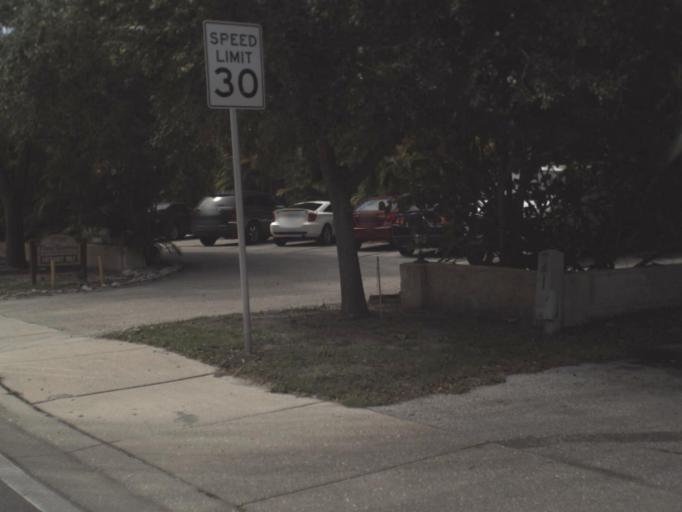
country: US
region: Florida
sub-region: Sarasota County
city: South Sarasota
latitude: 27.3013
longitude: -82.5337
